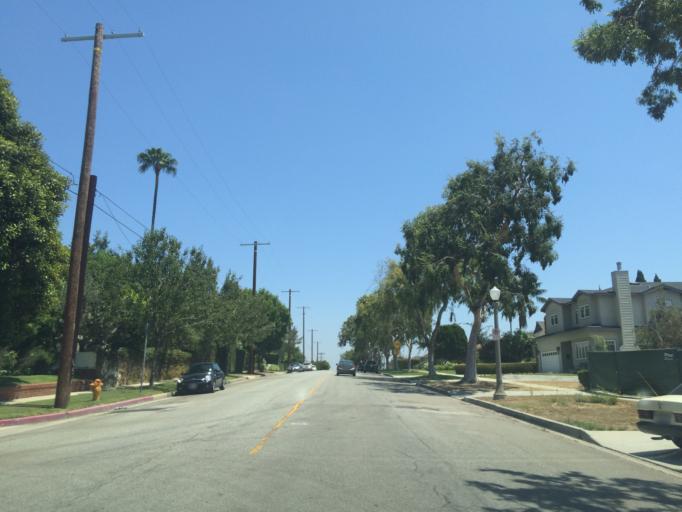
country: US
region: California
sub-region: Los Angeles County
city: Culver City
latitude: 34.0474
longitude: -118.3896
